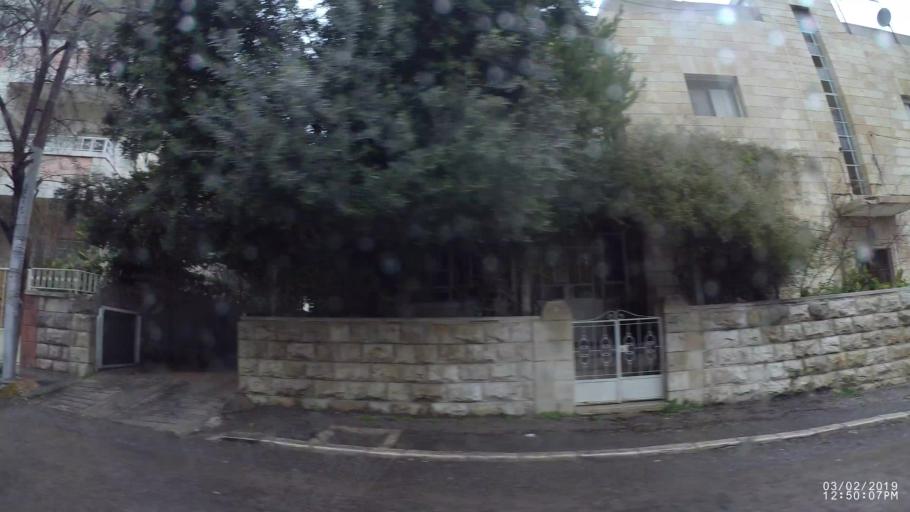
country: JO
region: Amman
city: Amman
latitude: 31.9588
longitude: 35.9145
